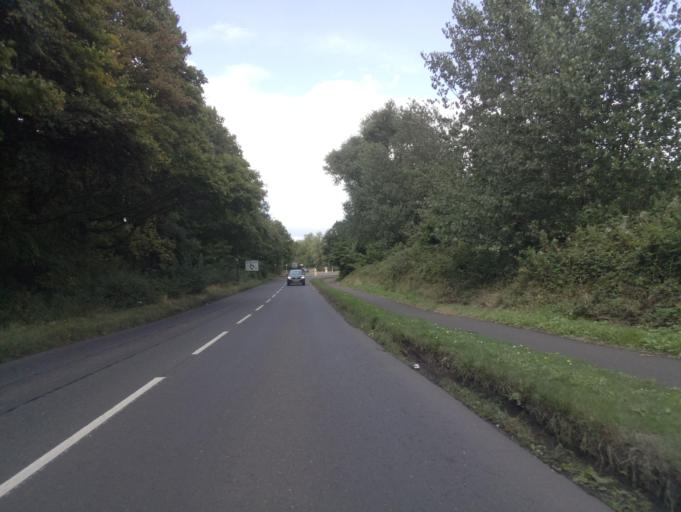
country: GB
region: Scotland
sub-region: East Lothian
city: Cockenzie
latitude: 55.9644
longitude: -2.9579
